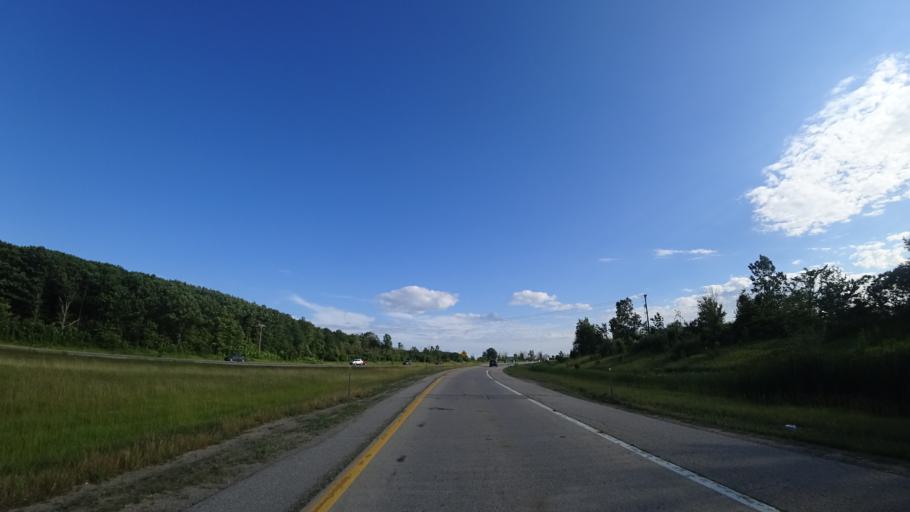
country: US
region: Michigan
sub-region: Ottawa County
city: Zeeland
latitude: 42.8094
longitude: -85.9840
